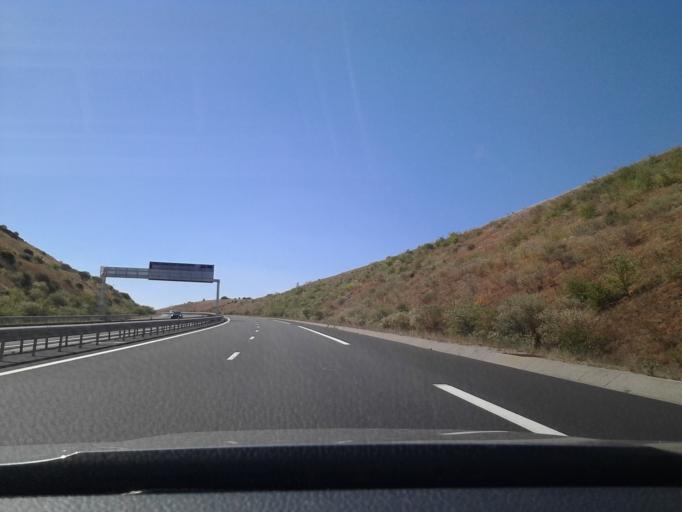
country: FR
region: Midi-Pyrenees
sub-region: Departement de l'Aveyron
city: Saint-Georges-de-Luzencon
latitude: 44.0631
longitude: 3.0266
